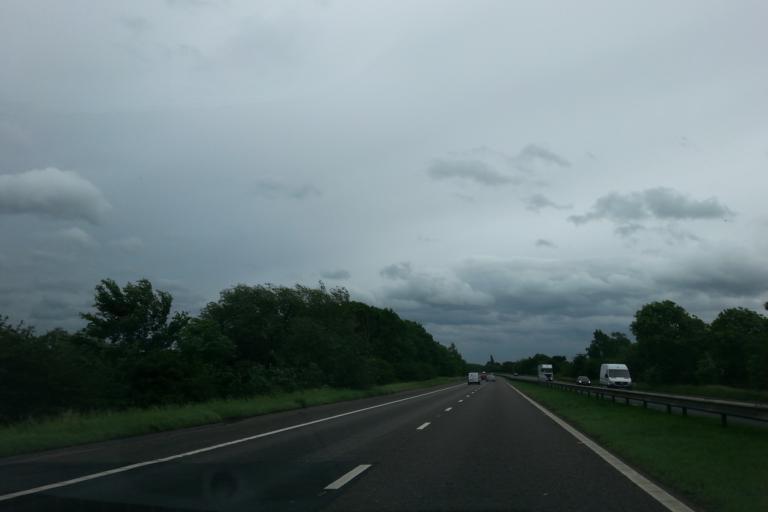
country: GB
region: England
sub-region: Doncaster
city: Tickhill
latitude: 53.4285
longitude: -1.0939
